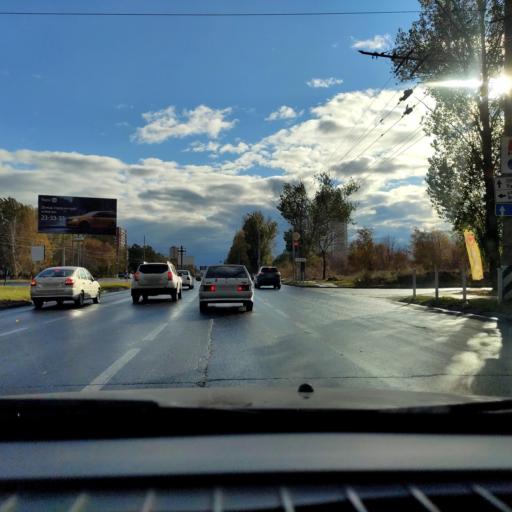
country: RU
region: Samara
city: Tol'yatti
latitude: 53.5176
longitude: 49.2583
